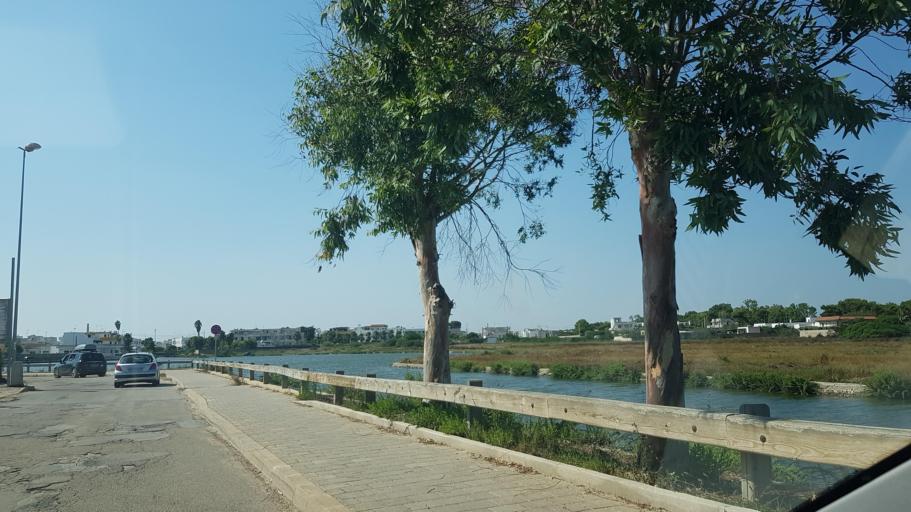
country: IT
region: Apulia
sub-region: Provincia di Lecce
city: Torre San Giovanni
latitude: 39.8882
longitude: 18.1196
